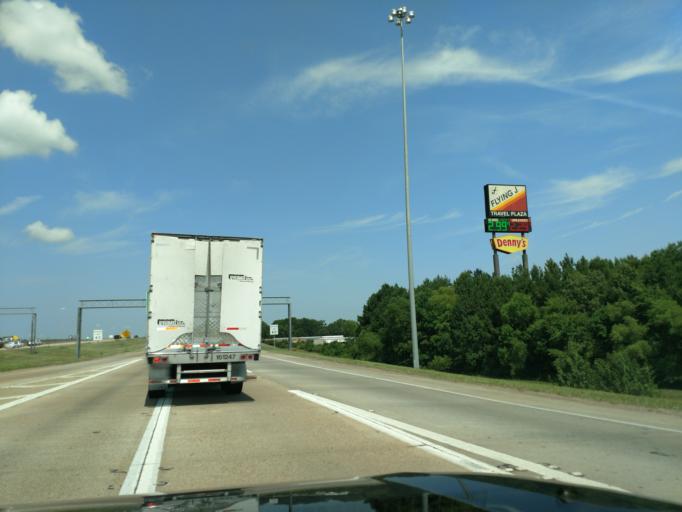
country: US
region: Mississippi
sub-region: Rankin County
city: Pearl
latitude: 32.2742
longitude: -90.1608
